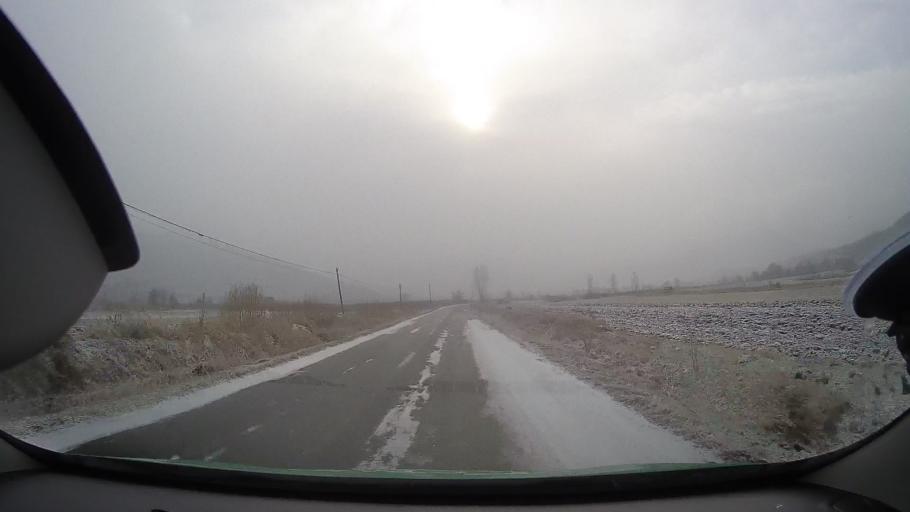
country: RO
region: Alba
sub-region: Comuna Rimetea
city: Rimetea
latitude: 46.4120
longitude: 23.5587
